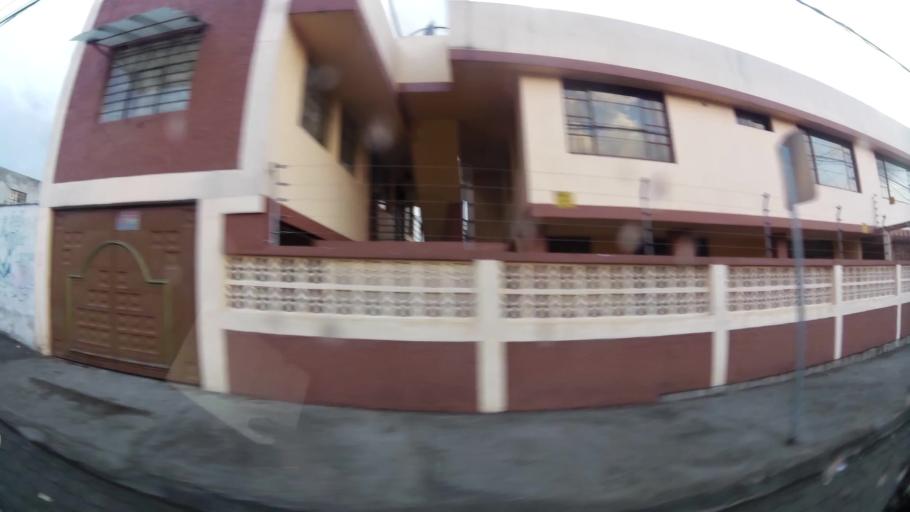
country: EC
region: Pichincha
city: Quito
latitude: -0.2956
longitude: -78.5379
